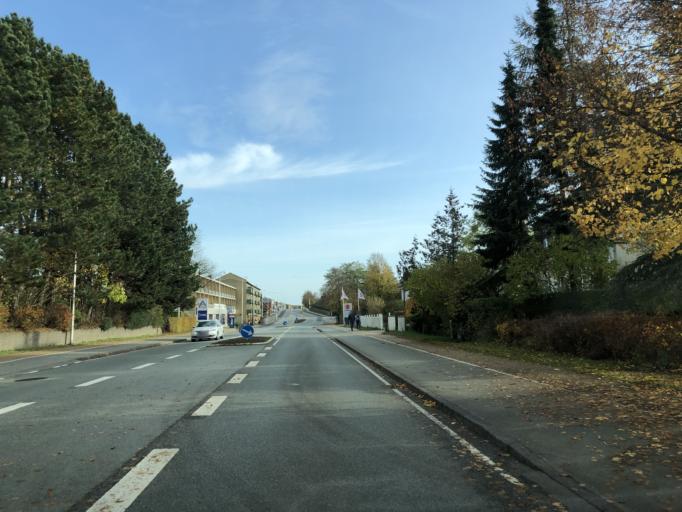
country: DK
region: Capital Region
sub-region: Rudersdal Kommune
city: Birkerod
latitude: 55.8452
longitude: 12.4322
